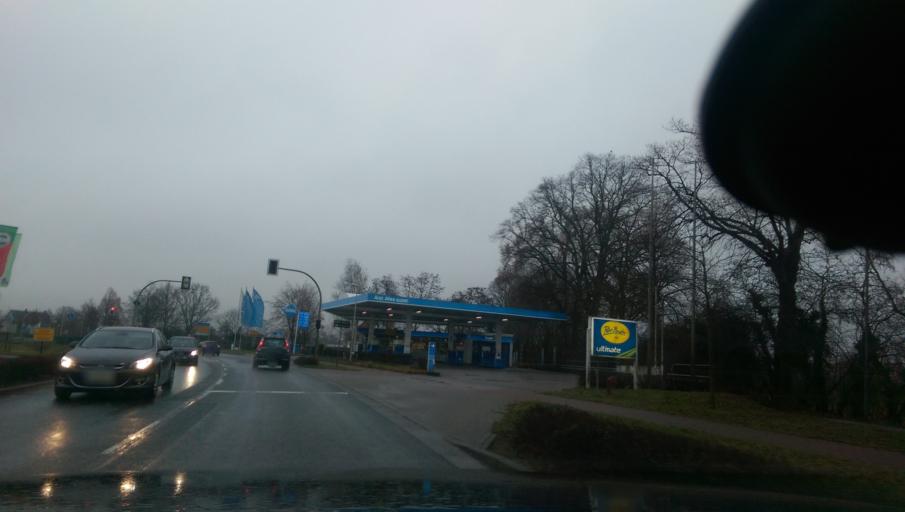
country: DE
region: Lower Saxony
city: Verden
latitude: 52.9176
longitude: 9.2192
